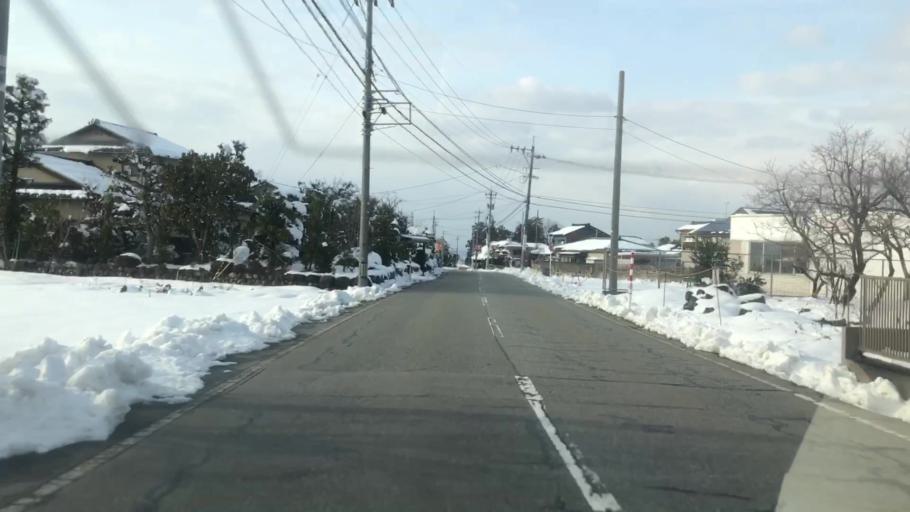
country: JP
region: Toyama
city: Toyama-shi
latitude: 36.6360
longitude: 137.2647
